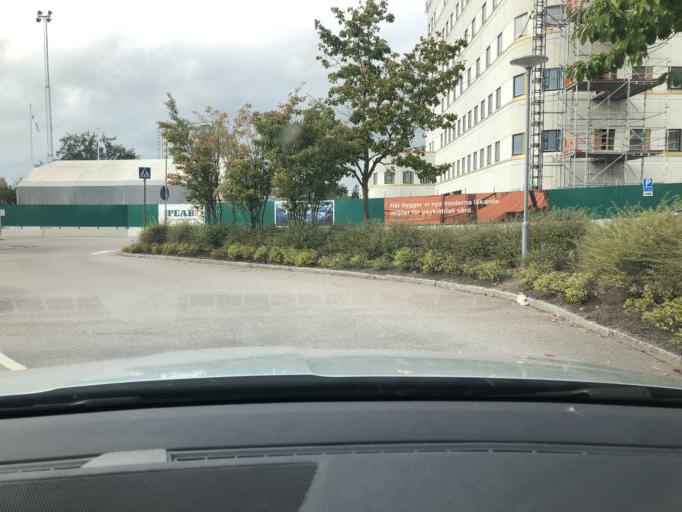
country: SE
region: Kalmar
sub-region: Kalmar Kommun
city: Kalmar
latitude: 56.6571
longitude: 16.3299
